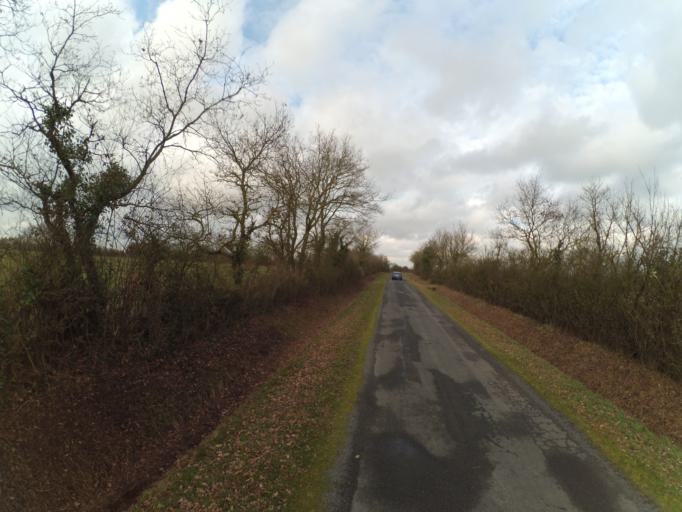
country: FR
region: Pays de la Loire
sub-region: Departement de la Loire-Atlantique
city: Saint-Hilaire-de-Clisson
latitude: 47.0448
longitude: -1.2915
